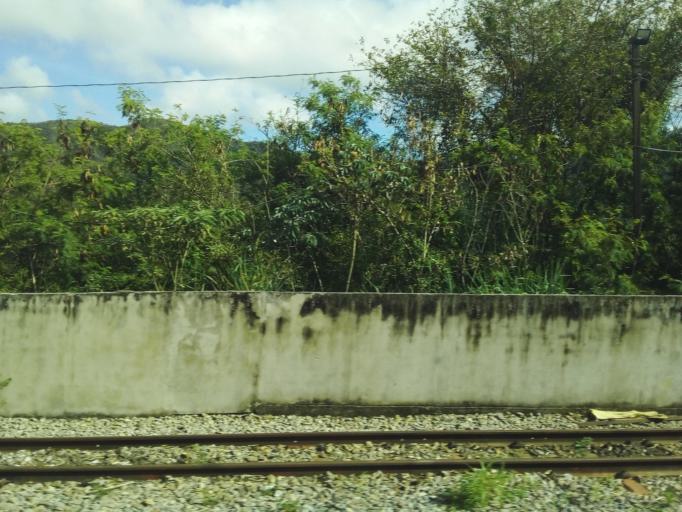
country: BR
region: Minas Gerais
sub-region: Raposos
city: Raposos
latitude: -19.8729
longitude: -43.7765
